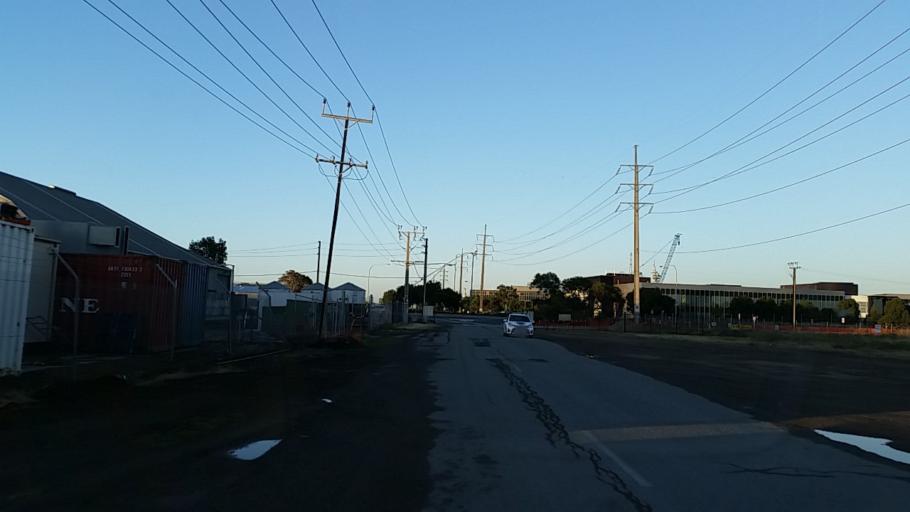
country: AU
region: South Australia
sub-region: Port Adelaide Enfield
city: Birkenhead
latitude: -34.7912
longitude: 138.5056
